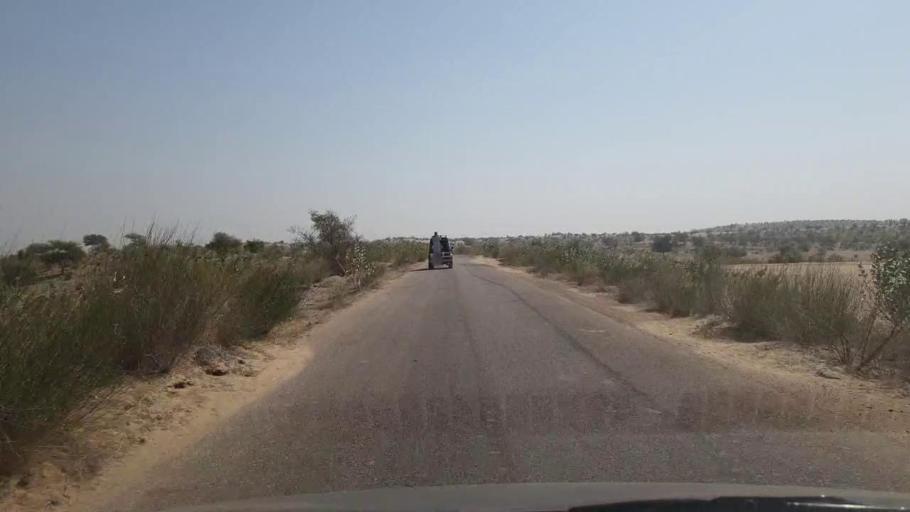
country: PK
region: Sindh
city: Chor
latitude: 25.5991
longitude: 70.0069
